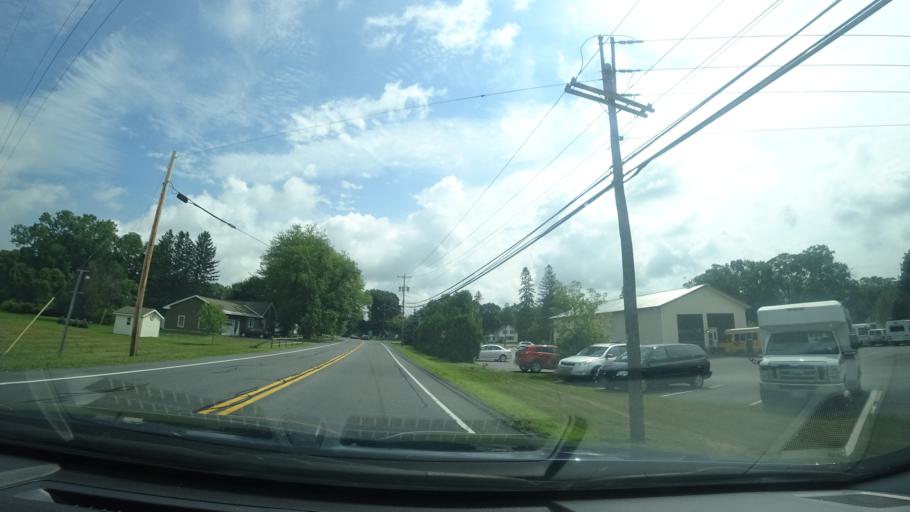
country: US
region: New York
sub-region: Washington County
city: Hudson Falls
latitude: 43.3169
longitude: -73.5986
